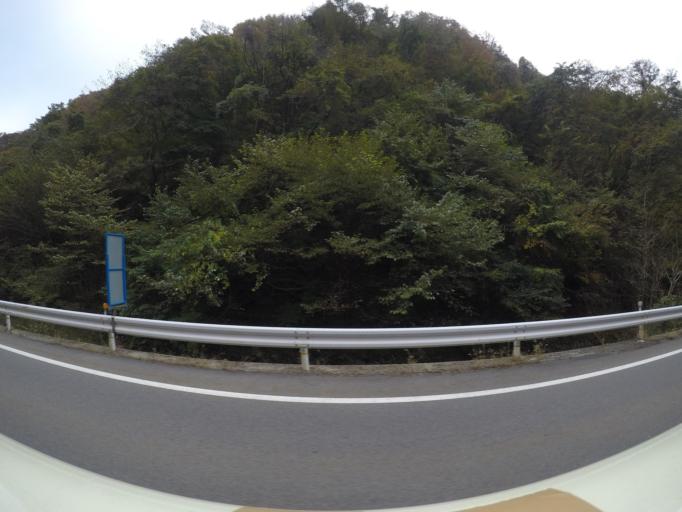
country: JP
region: Nagano
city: Ina
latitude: 35.9135
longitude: 137.7832
